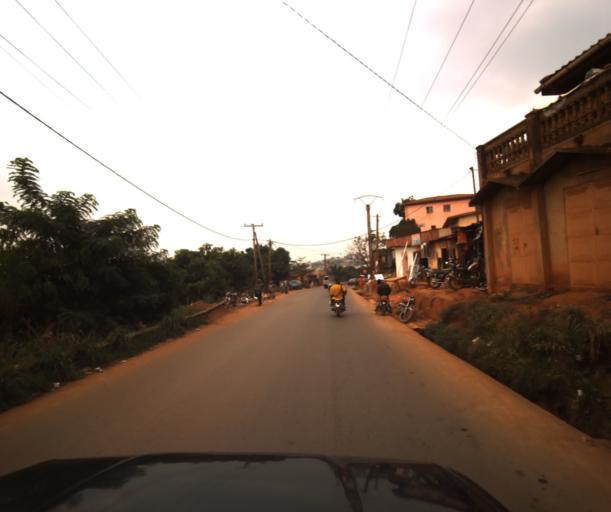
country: CM
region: Centre
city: Yaounde
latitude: 3.8469
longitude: 11.4798
